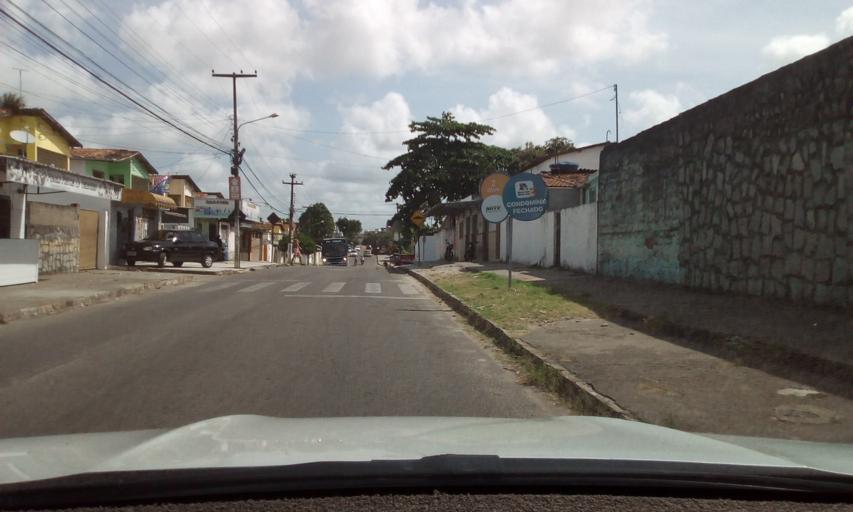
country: BR
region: Paraiba
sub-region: Joao Pessoa
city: Joao Pessoa
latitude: -7.1692
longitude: -34.8879
